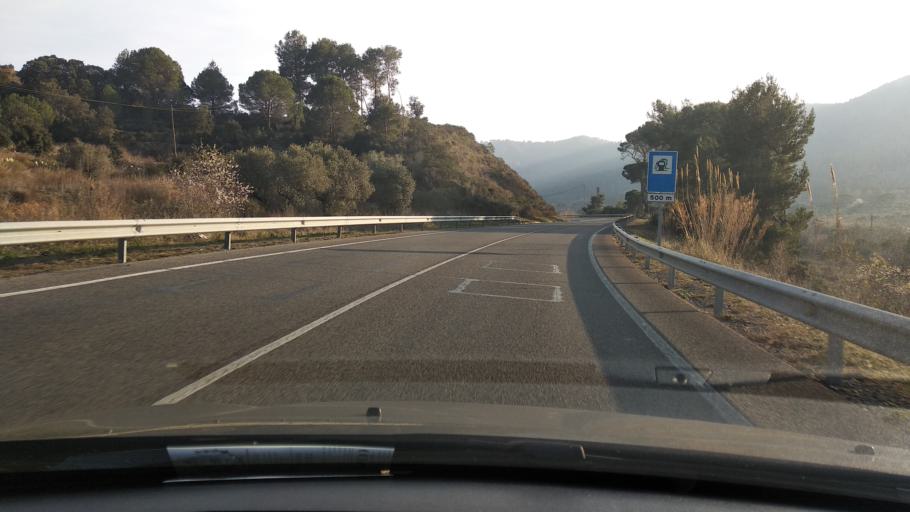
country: ES
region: Catalonia
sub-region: Provincia de Tarragona
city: Alforja
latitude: 41.1969
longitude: 0.9983
